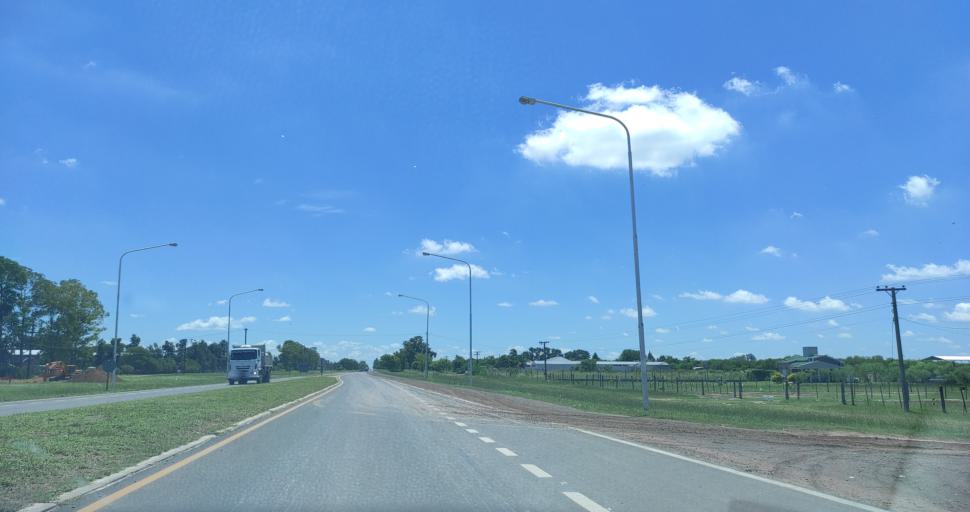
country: AR
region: Chaco
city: Las Brenas
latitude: -27.1128
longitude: -61.0779
